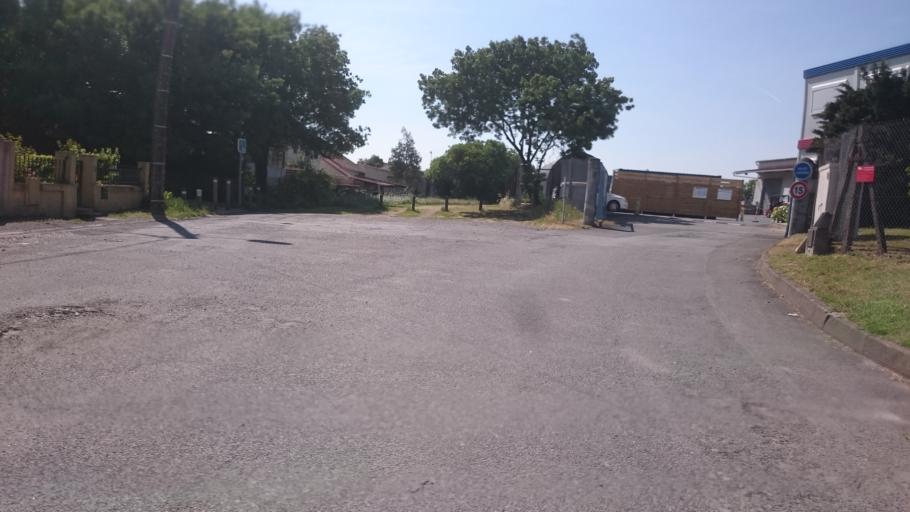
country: FR
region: Pays de la Loire
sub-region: Departement de la Loire-Atlantique
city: Bouguenais
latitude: 47.1869
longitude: -1.5888
